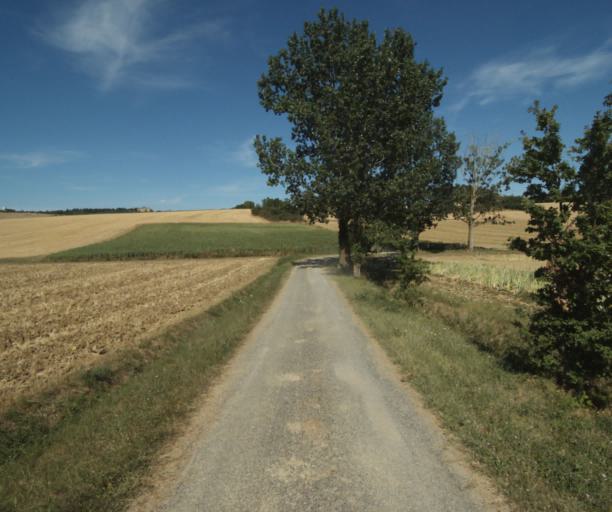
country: FR
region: Midi-Pyrenees
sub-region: Departement de la Haute-Garonne
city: Saint-Felix-Lauragais
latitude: 43.5006
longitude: 1.9255
